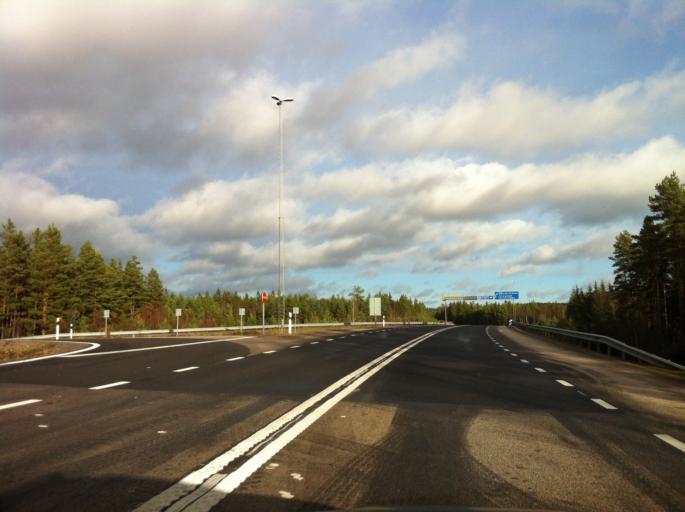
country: SE
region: Kronoberg
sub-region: Vaxjo Kommun
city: Braas
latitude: 57.0785
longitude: 15.1713
